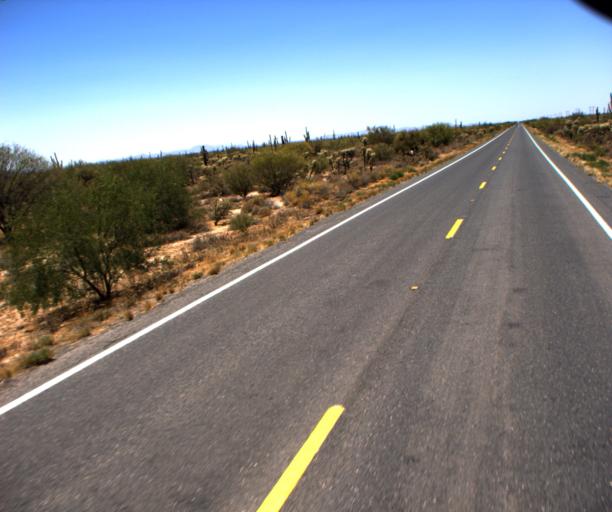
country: US
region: Arizona
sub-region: Pinal County
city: Florence
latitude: 32.8526
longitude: -111.2328
